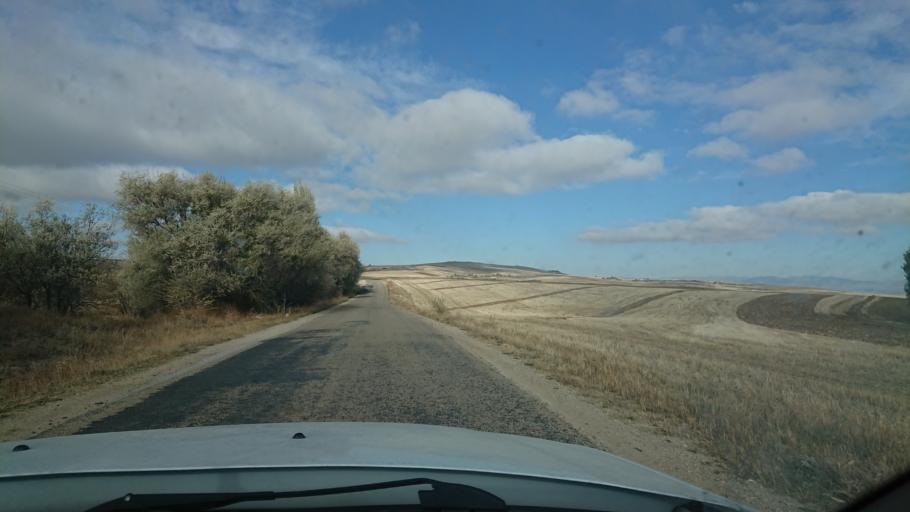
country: TR
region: Aksaray
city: Agacoren
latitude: 38.8149
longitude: 33.9825
